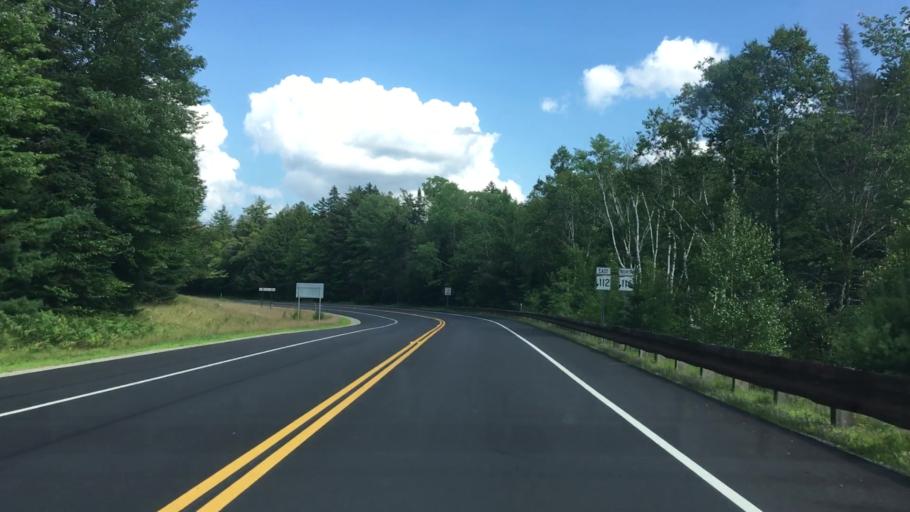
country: US
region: New Hampshire
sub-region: Grafton County
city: North Haverhill
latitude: 44.0980
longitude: -71.8478
